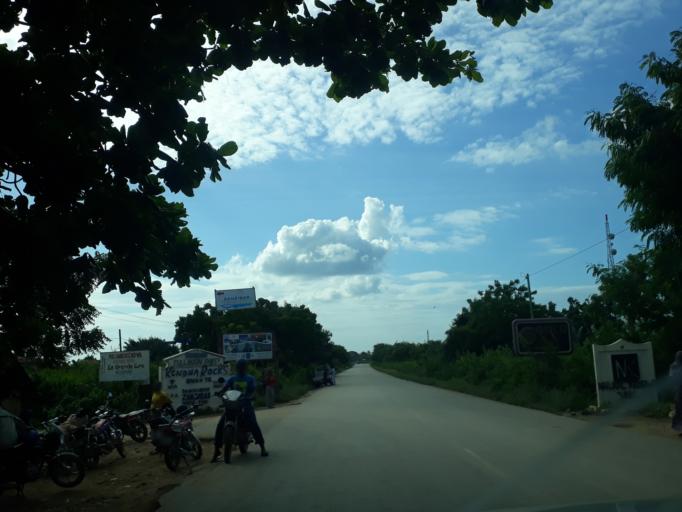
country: TZ
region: Zanzibar North
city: Nungwi
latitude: -5.7569
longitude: 39.3011
